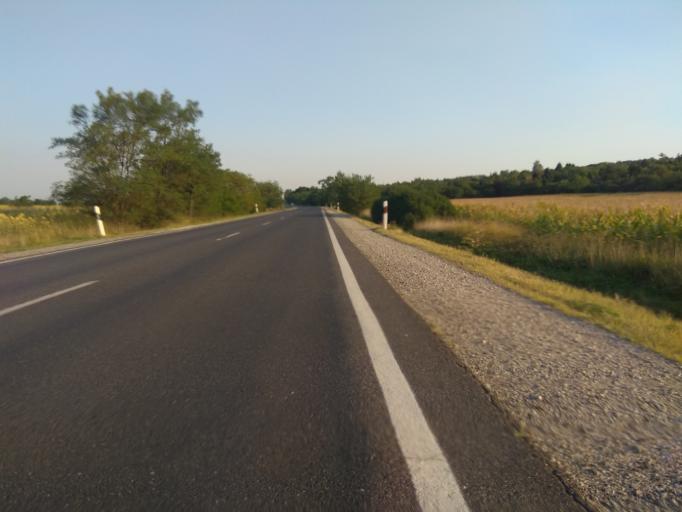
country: HU
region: Borsod-Abauj-Zemplen
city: Nyekladhaza
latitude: 47.9713
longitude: 20.8309
